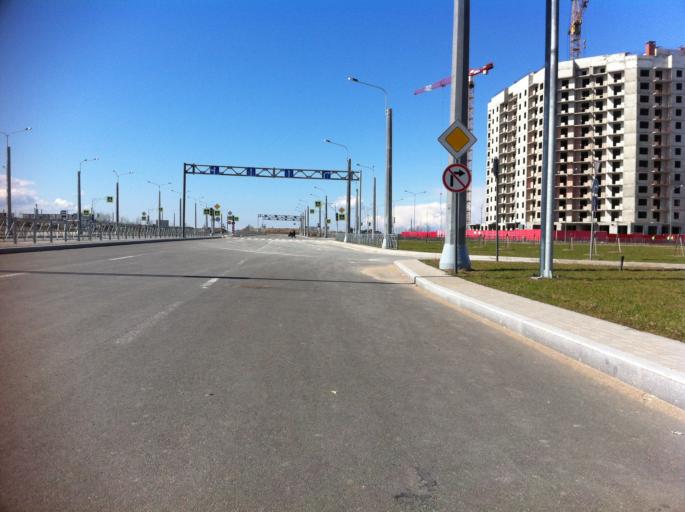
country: RU
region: St.-Petersburg
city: Uritsk
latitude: 59.8662
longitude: 30.1587
